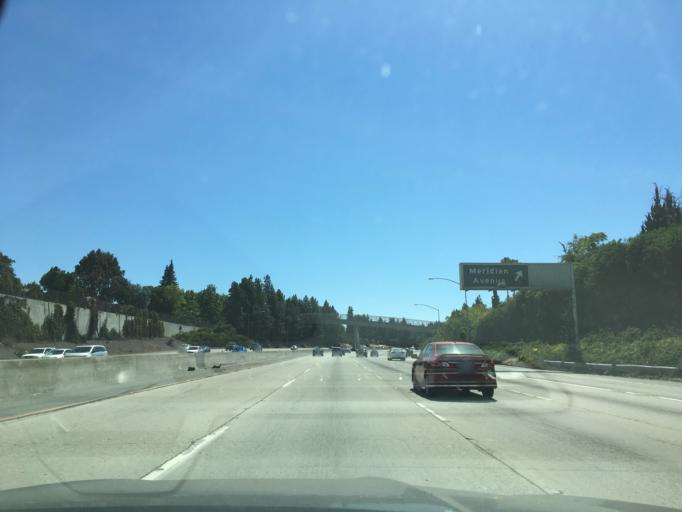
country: US
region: California
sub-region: Santa Clara County
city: Buena Vista
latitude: 37.3168
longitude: -121.9224
